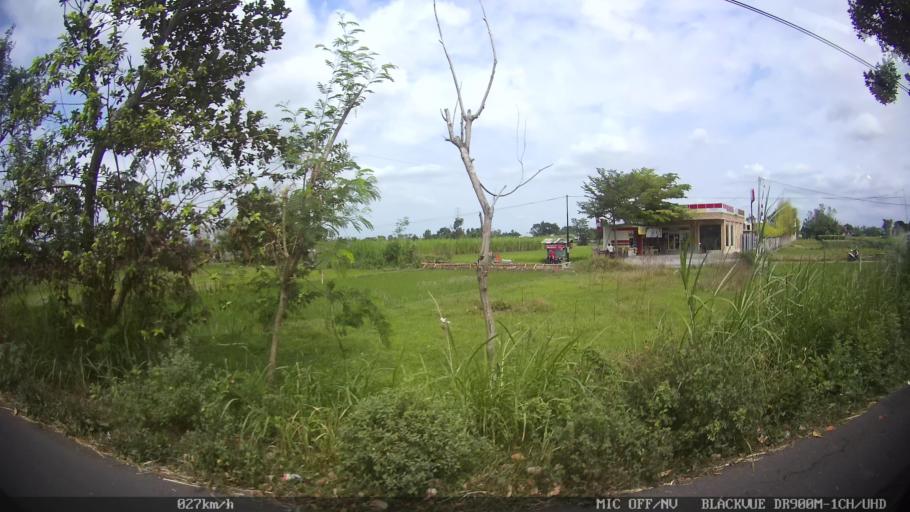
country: ID
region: Central Java
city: Candi Prambanan
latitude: -7.7872
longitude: 110.4807
